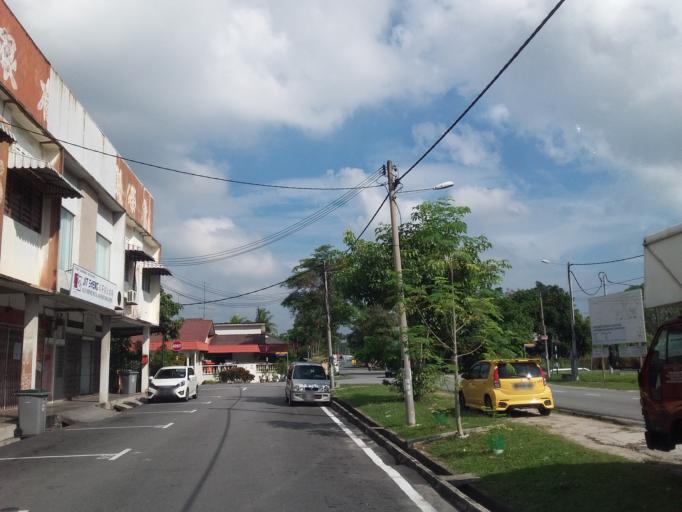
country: MY
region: Johor
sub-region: Daerah Batu Pahat
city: Batu Pahat
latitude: 1.8424
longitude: 102.9267
